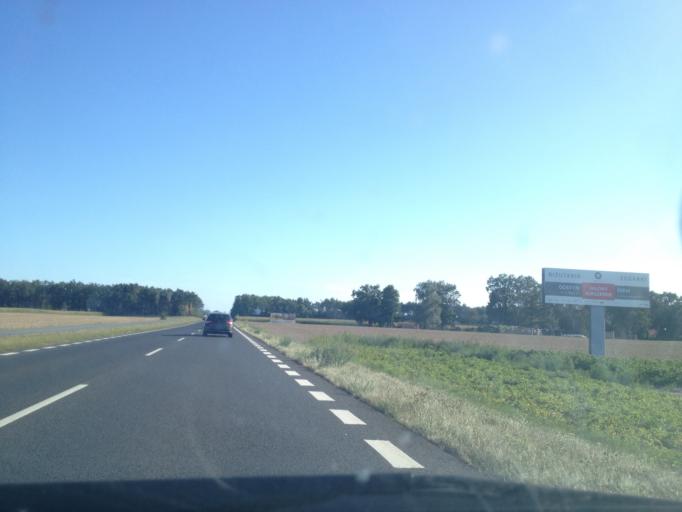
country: PL
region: Greater Poland Voivodeship
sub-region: Powiat sremski
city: Srem
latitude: 52.1191
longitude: 17.0437
